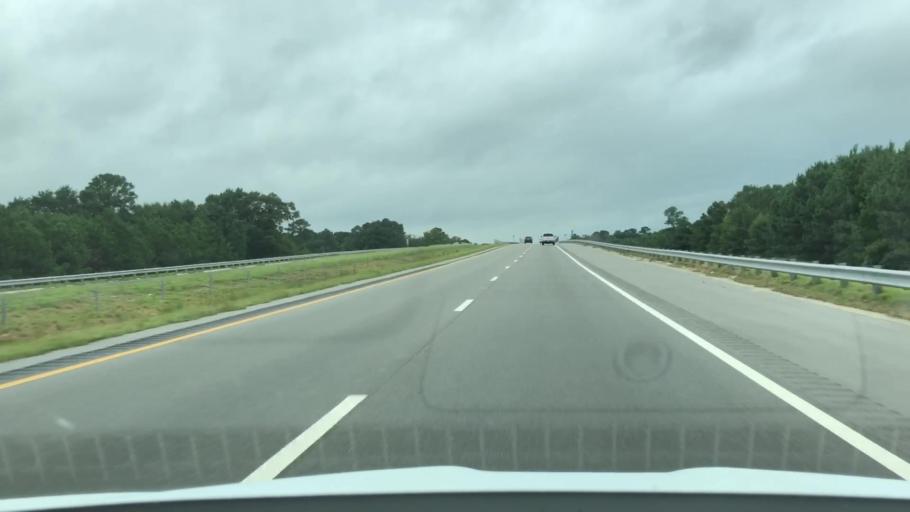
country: US
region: North Carolina
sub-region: Wayne County
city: Elroy
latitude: 35.3394
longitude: -77.8445
